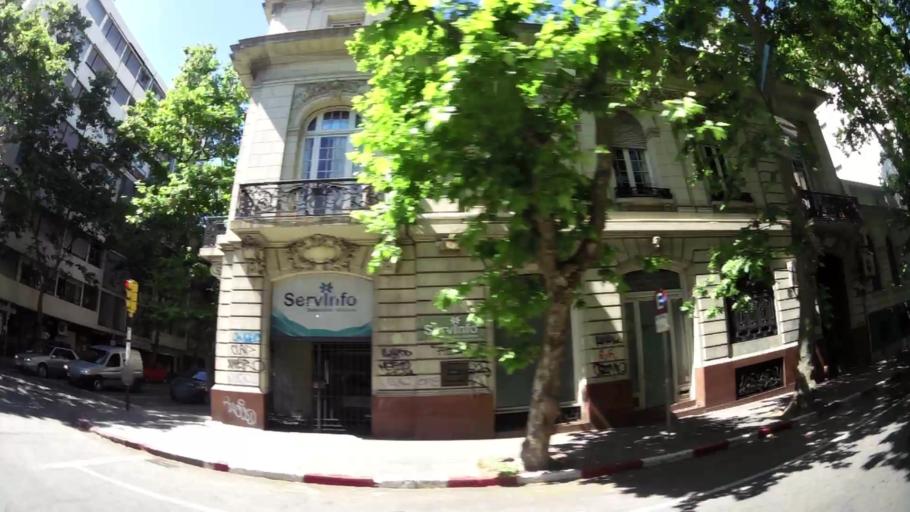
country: UY
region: Montevideo
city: Montevideo
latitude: -34.9029
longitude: -56.1896
